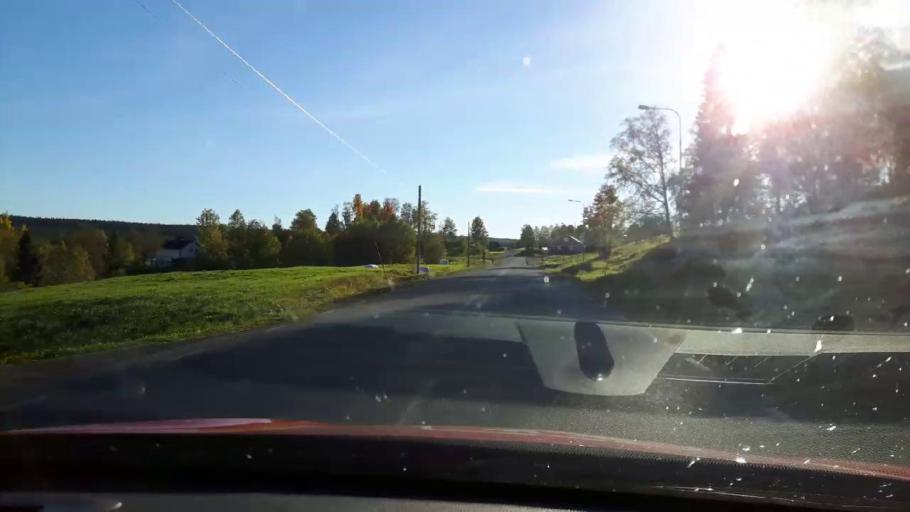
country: SE
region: Jaemtland
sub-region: OEstersunds Kommun
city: Lit
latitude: 63.8168
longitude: 14.8114
